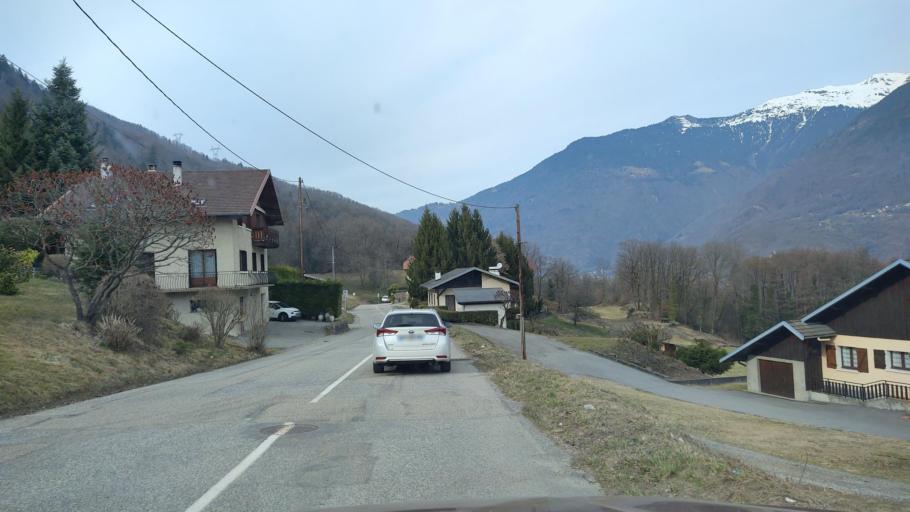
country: FR
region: Rhone-Alpes
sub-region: Departement de la Savoie
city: La Bathie
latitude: 45.6187
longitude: 6.4334
